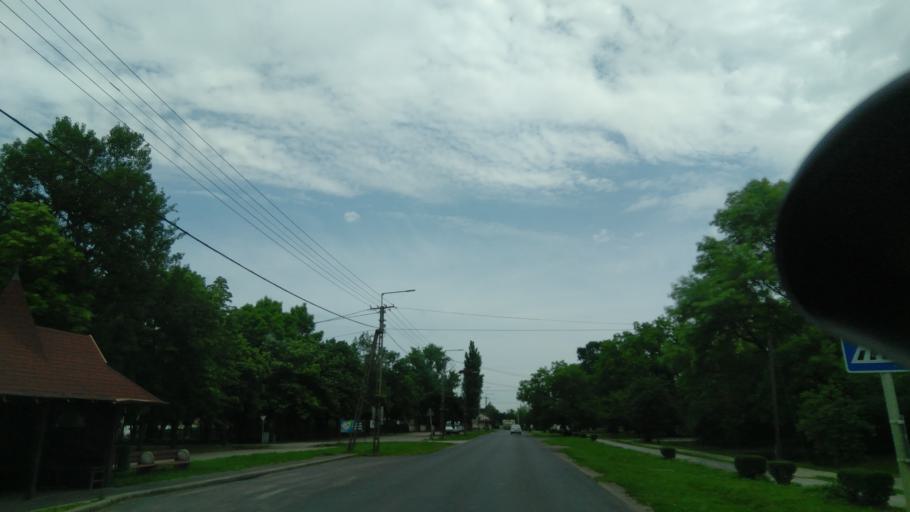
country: HU
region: Bekes
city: Fuzesgyarmat
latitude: 47.0950
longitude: 21.2058
